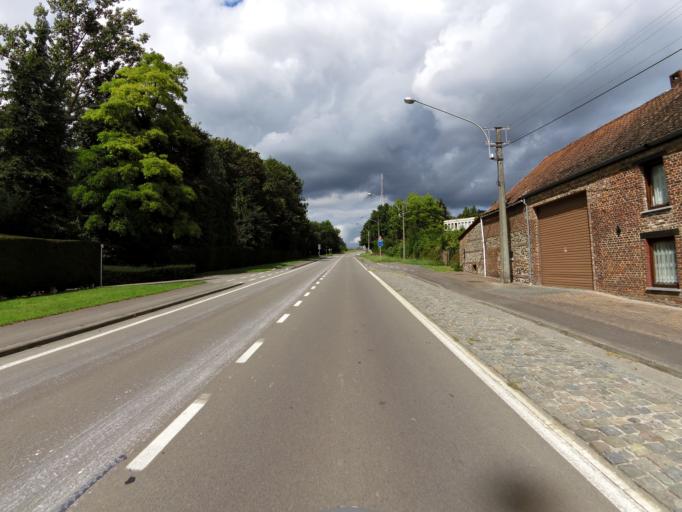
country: BE
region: Wallonia
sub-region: Province du Hainaut
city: Chasse Royale
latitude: 50.4111
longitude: 4.0085
